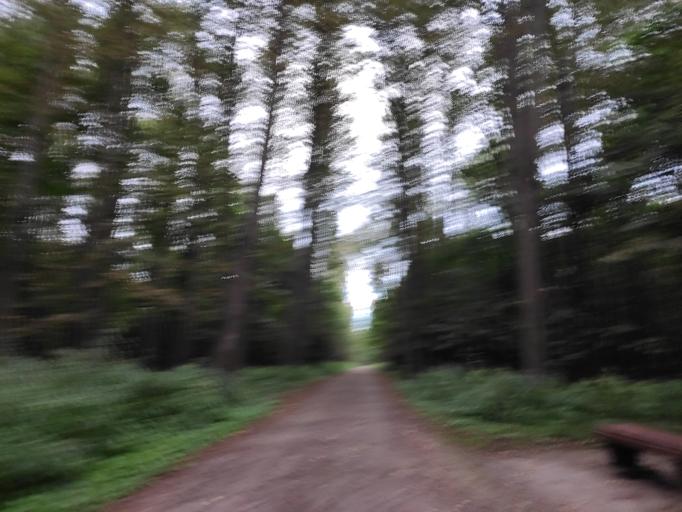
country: RU
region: Moskovskaya
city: Izmaylovo
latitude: 55.7670
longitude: 37.7895
